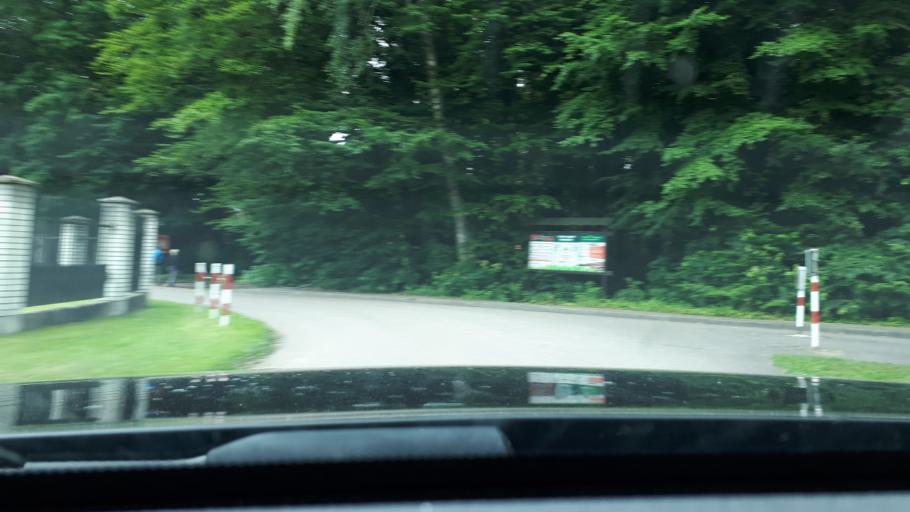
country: PL
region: Warmian-Masurian Voivodeship
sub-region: Powiat ostrodzki
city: Ostroda
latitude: 53.6894
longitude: 20.0971
